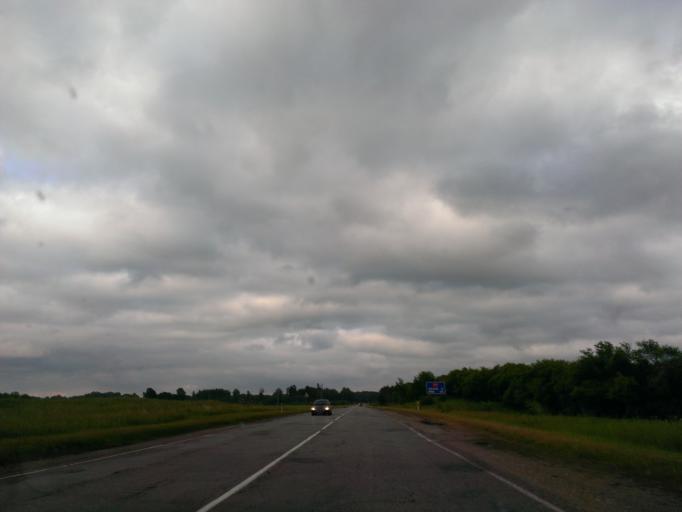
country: LV
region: Skrunda
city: Skrunda
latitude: 56.6761
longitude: 22.2405
